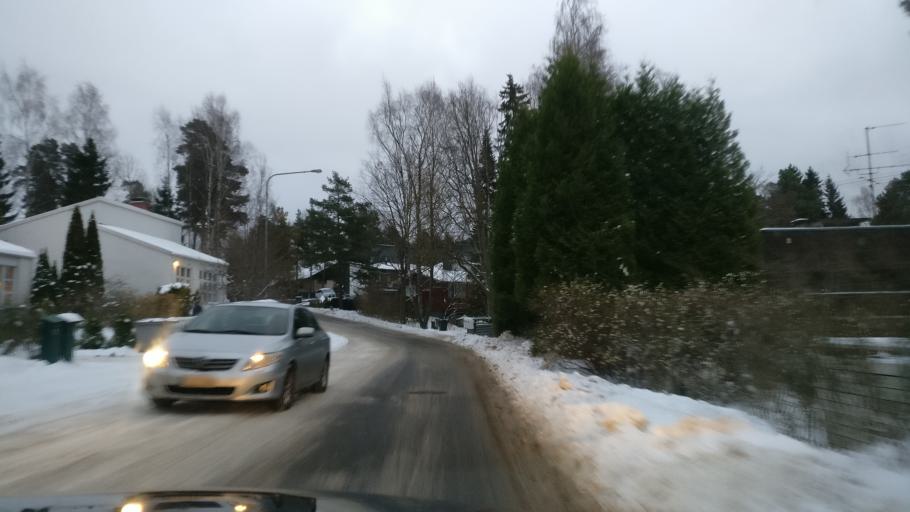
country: FI
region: Uusimaa
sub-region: Helsinki
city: Vantaa
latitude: 60.1643
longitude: 25.0770
